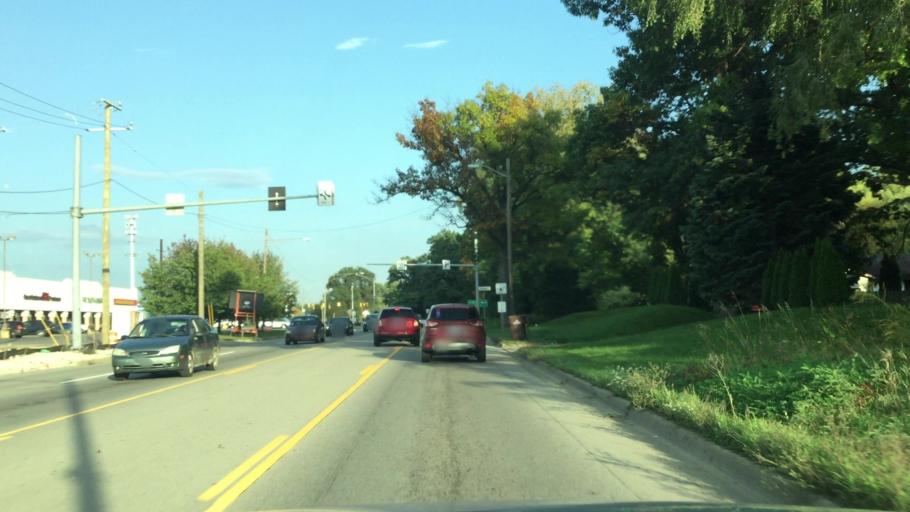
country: US
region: Michigan
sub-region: Oakland County
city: Wolverine Lake
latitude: 42.6143
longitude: -83.4452
